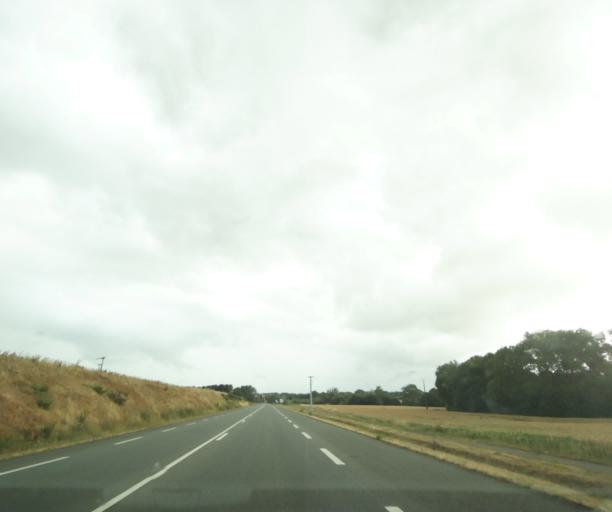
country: FR
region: Pays de la Loire
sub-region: Departement de la Vendee
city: Saint-Hilaire-de-Talmont
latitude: 46.4621
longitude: -1.6031
